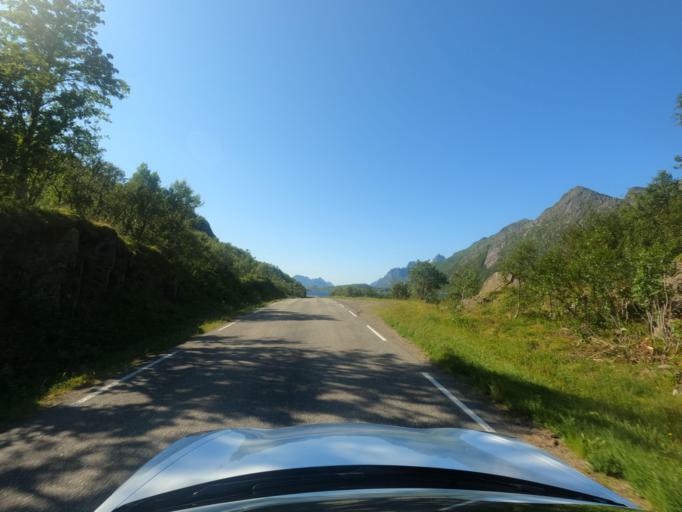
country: NO
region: Nordland
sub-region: Hadsel
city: Stokmarknes
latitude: 68.3867
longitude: 15.0939
